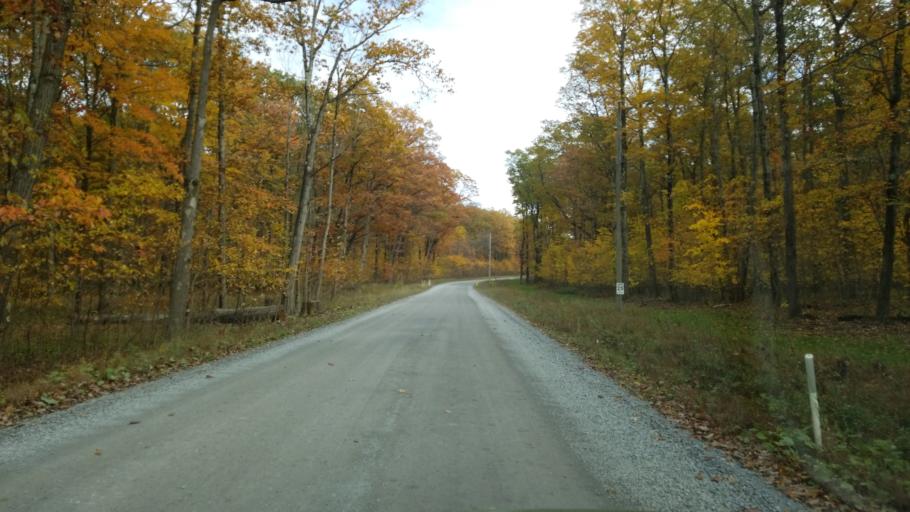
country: US
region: Pennsylvania
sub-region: Clearfield County
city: Clearfield
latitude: 41.1420
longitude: -78.5006
